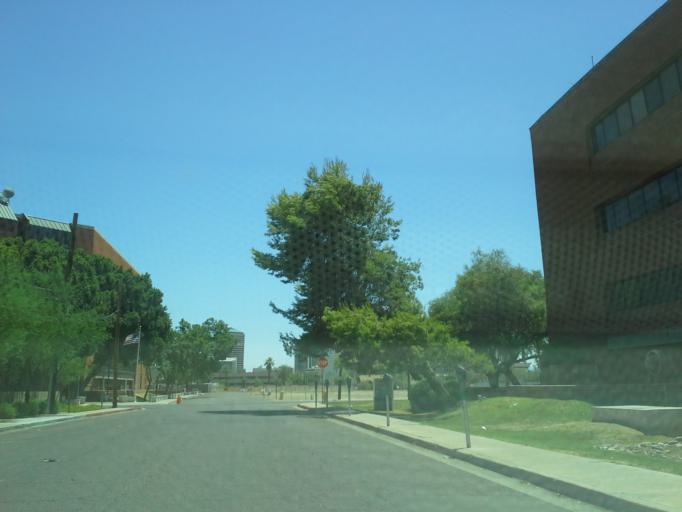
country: US
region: Arizona
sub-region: Maricopa County
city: Phoenix
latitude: 33.4929
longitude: -112.0717
